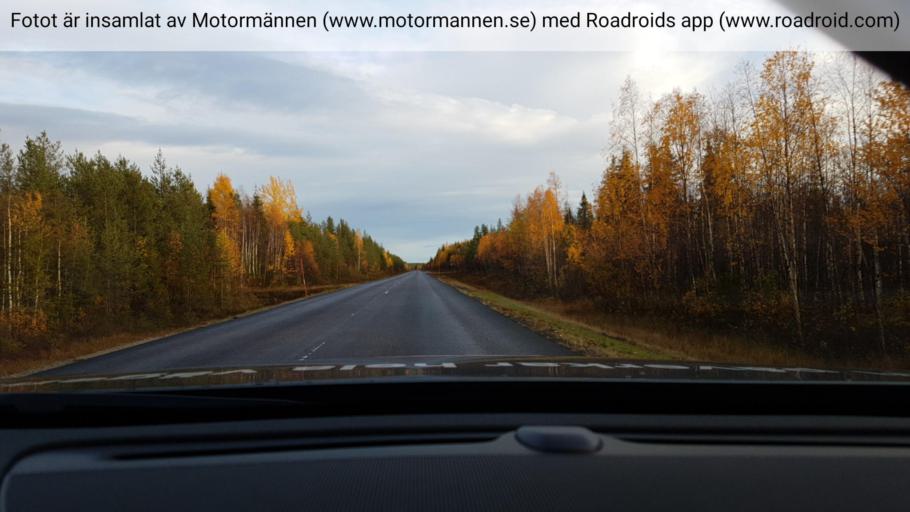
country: SE
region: Norrbotten
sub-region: Overkalix Kommun
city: OEverkalix
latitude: 67.0001
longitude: 22.5607
